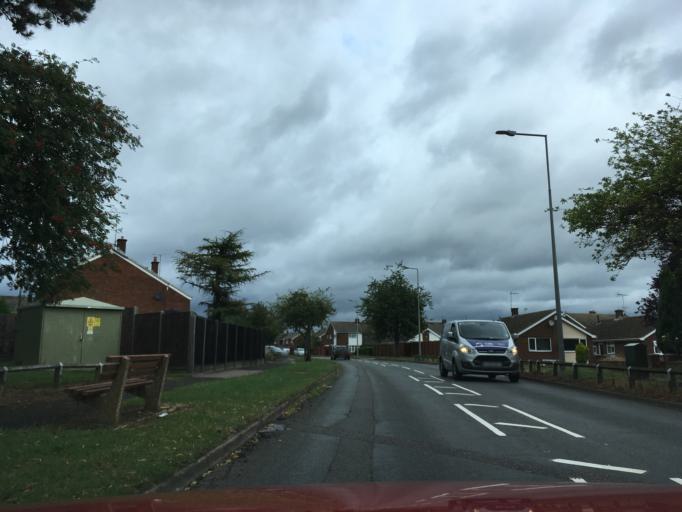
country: GB
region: England
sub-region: Buckinghamshire
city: Bletchley
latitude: 52.0039
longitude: -0.7414
